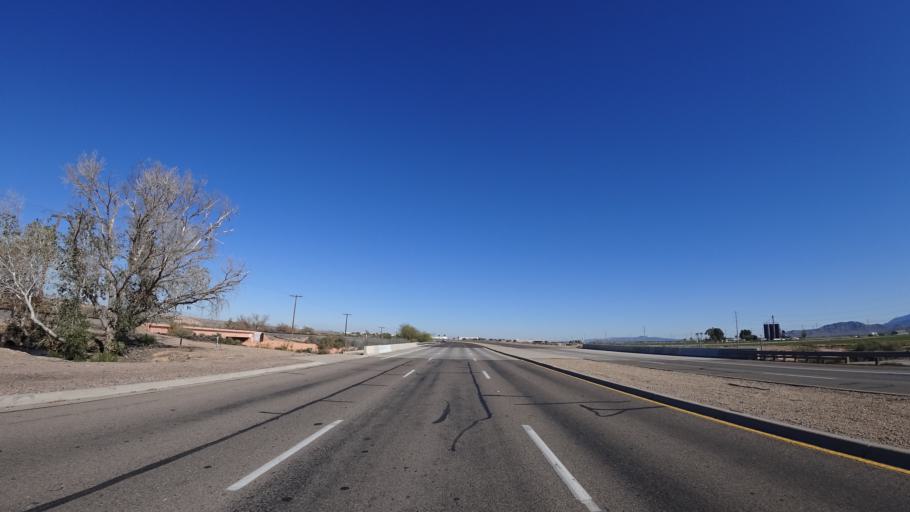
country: US
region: Arizona
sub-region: Maricopa County
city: Goodyear
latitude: 33.4094
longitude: -112.3876
